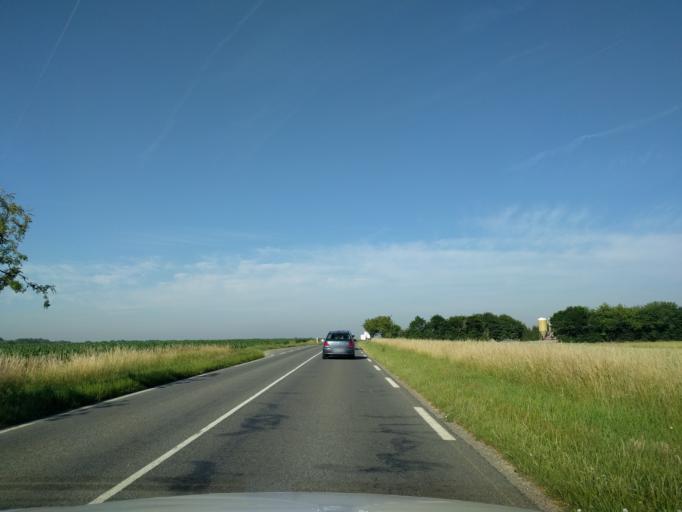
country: FR
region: Picardie
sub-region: Departement de la Somme
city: Montdidier
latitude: 49.6407
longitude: 2.5519
